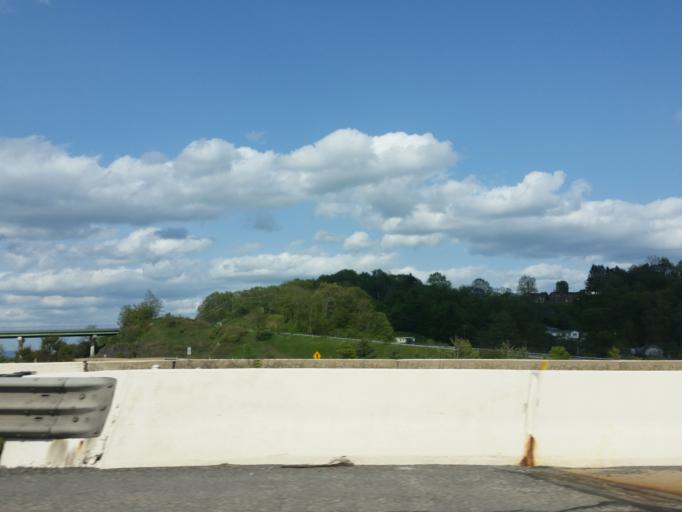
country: US
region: West Virginia
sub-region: Raleigh County
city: MacArthur
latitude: 37.7588
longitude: -81.2131
